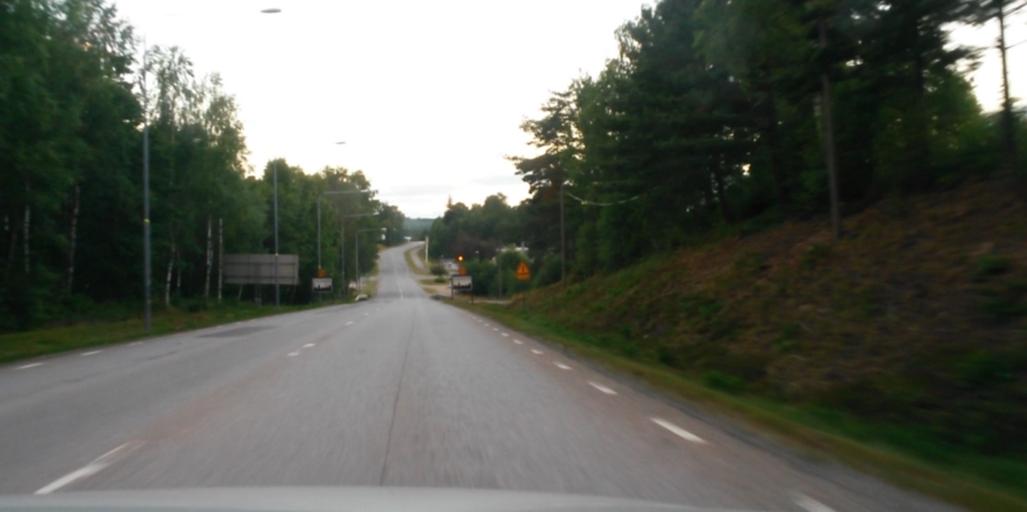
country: SE
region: Vaestra Goetaland
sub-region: Tranemo Kommun
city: Tranemo
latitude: 57.4886
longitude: 13.3595
